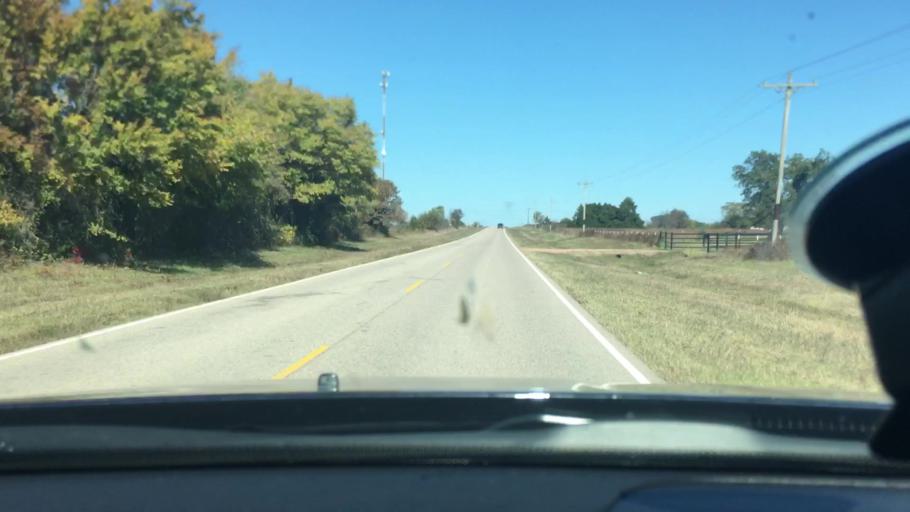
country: US
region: Oklahoma
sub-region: Johnston County
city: Tishomingo
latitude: 34.4276
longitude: -96.6364
